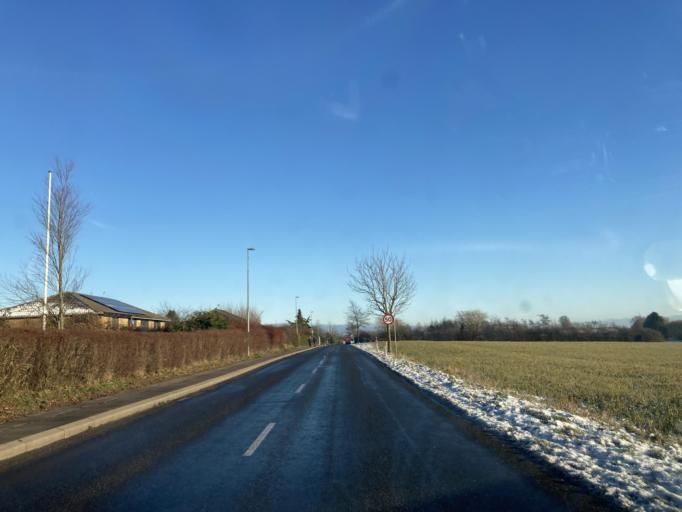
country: DK
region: South Denmark
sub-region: Svendborg Kommune
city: Thuro By
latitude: 55.1447
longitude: 10.6972
